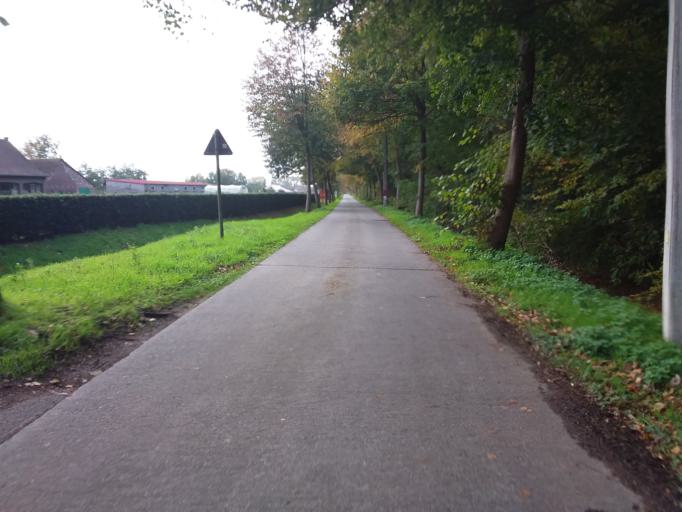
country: BE
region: Flanders
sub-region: Provincie Oost-Vlaanderen
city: Zulte
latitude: 50.9391
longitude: 3.4760
